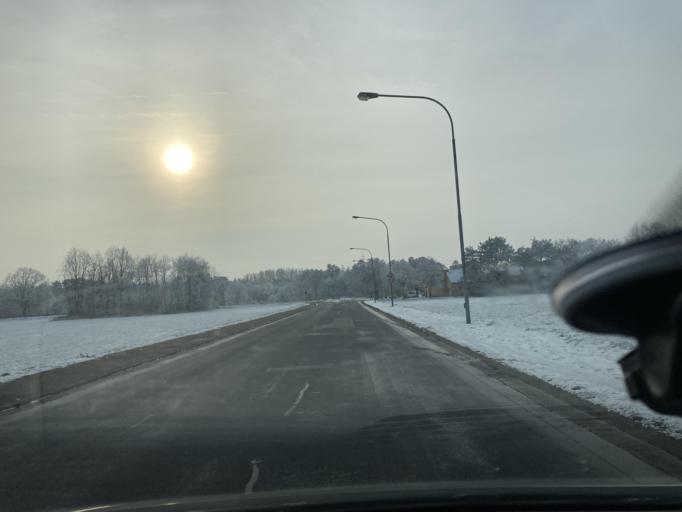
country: DE
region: Hesse
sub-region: Regierungsbezirk Darmstadt
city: Muehlheim am Main
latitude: 50.1116
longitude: 8.8278
